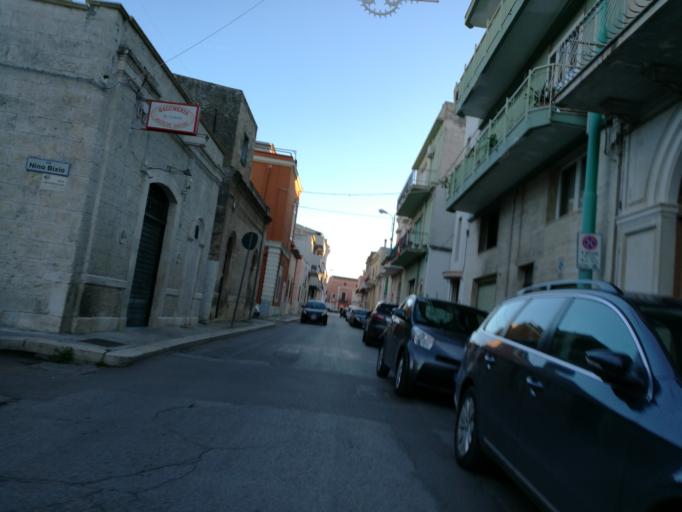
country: IT
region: Apulia
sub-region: Provincia di Bari
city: Adelfia
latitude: 41.0059
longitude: 16.8777
